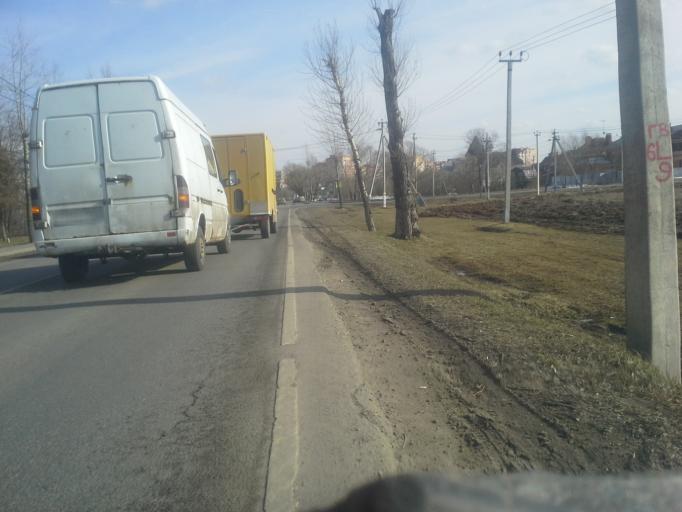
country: RU
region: Moskovskaya
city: Shcherbinka
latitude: 55.4748
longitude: 37.5345
